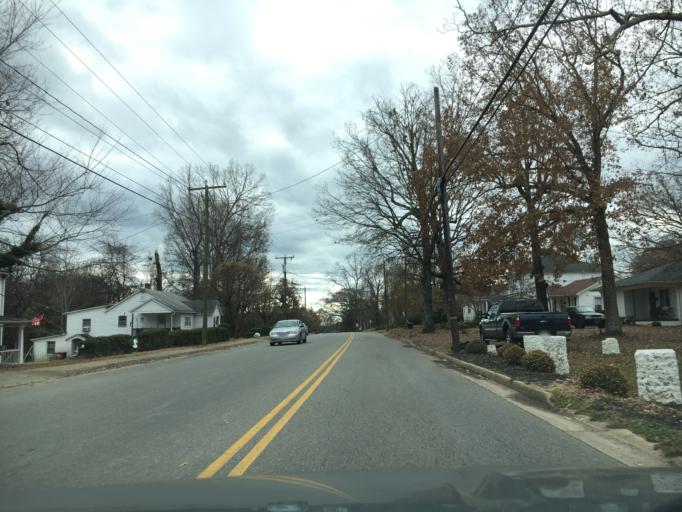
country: US
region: Virginia
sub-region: Halifax County
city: South Boston
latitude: 36.7163
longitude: -78.9024
